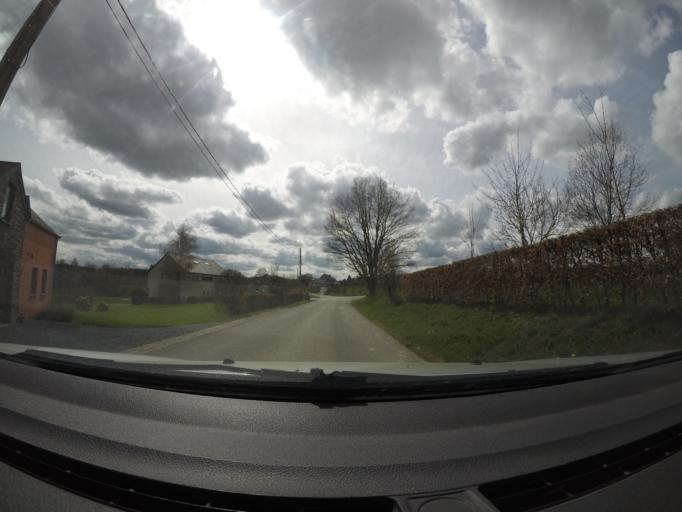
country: BE
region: Wallonia
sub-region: Province du Luxembourg
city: Leglise
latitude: 49.7975
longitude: 5.4817
